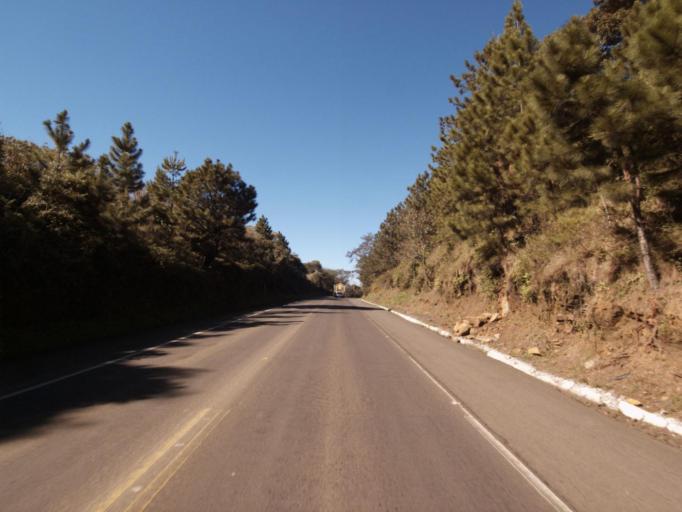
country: BR
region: Santa Catarina
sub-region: Sao Lourenco Do Oeste
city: Sao Lourenco dOeste
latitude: -26.8085
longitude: -53.1702
